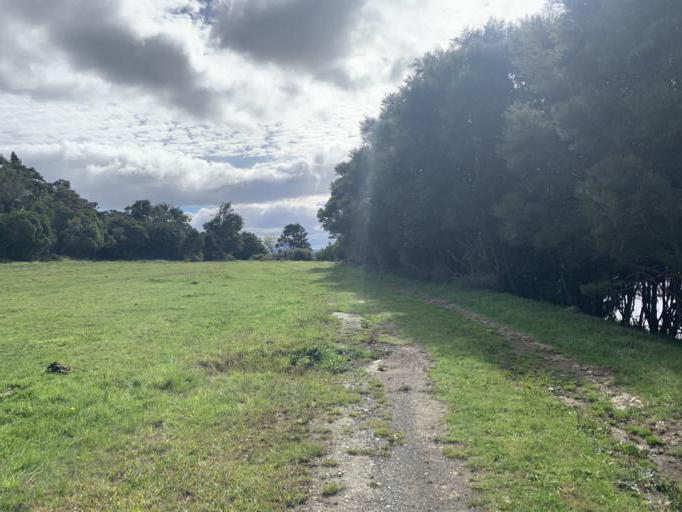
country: NZ
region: Waikato
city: Turangi
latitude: -38.9748
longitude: 175.7775
